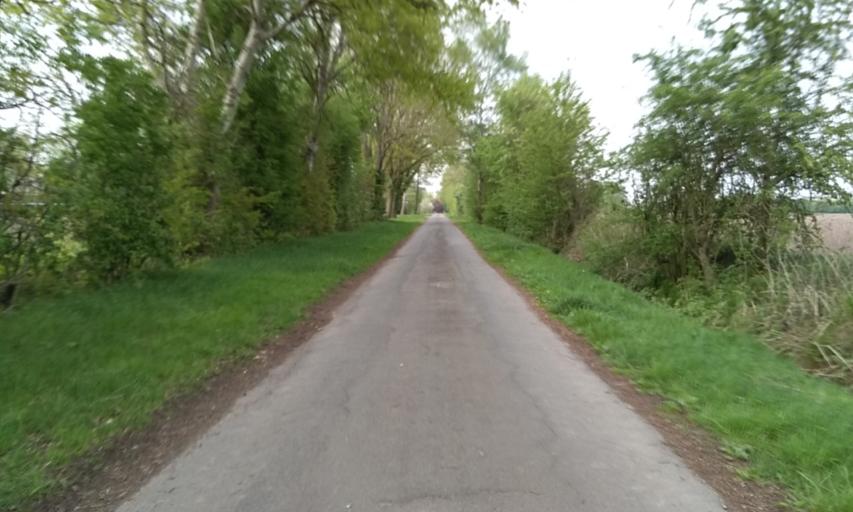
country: DE
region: Lower Saxony
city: Bliedersdorf
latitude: 53.4505
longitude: 9.5675
